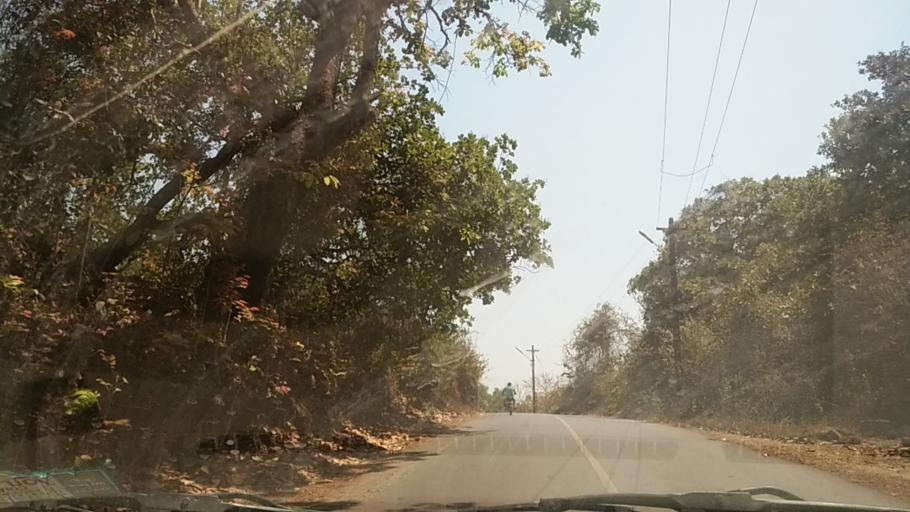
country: IN
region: Goa
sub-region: North Goa
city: Dicholi
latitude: 15.5822
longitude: 73.9367
